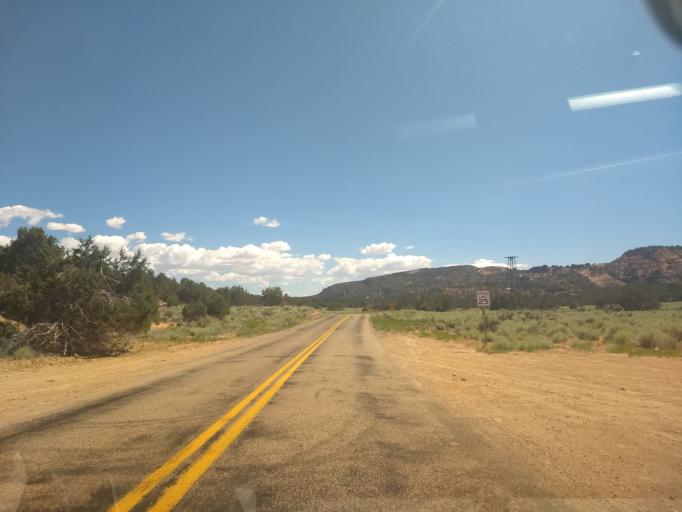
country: US
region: Utah
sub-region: Washington County
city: Hildale
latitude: 37.0002
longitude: -112.8616
